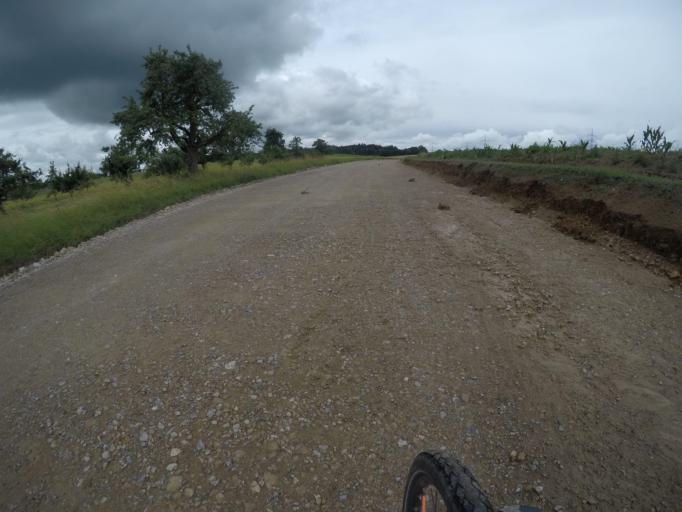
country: DE
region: Baden-Wuerttemberg
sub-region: Regierungsbezirk Stuttgart
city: Deckenpfronn
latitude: 48.6122
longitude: 8.8259
